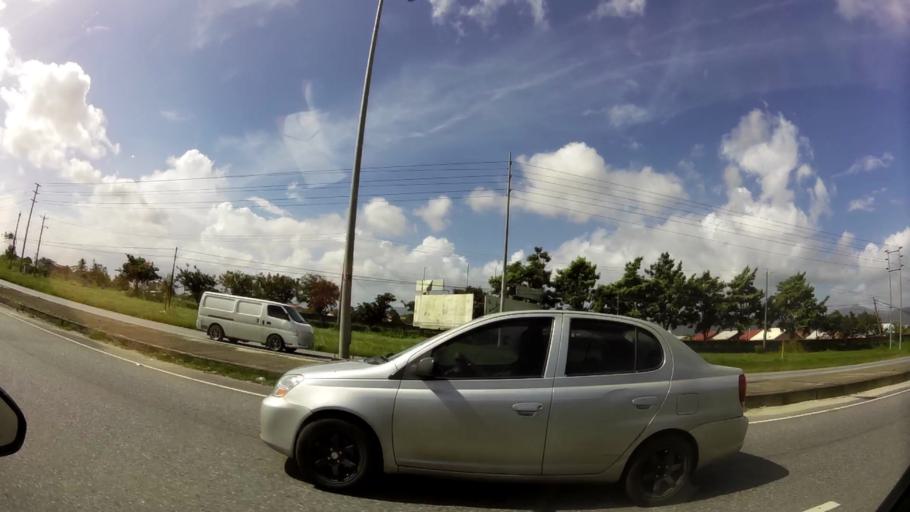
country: TT
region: Borough of Arima
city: Arima
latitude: 10.6092
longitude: -61.2673
